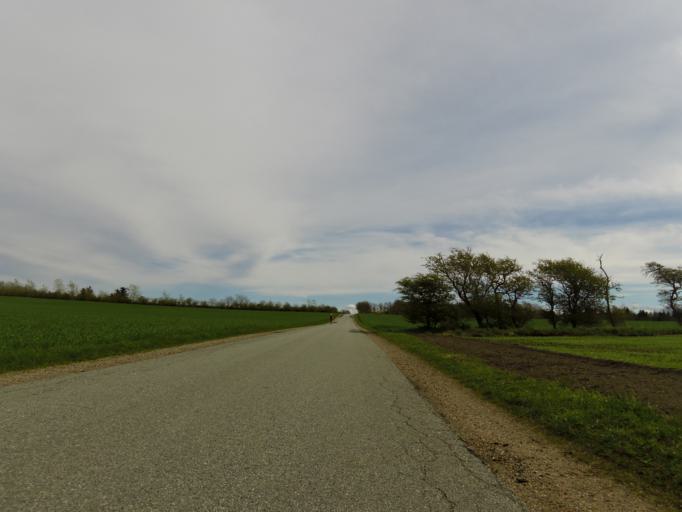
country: DK
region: Central Jutland
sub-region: Holstebro Kommune
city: Vinderup
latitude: 56.5379
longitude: 8.8842
